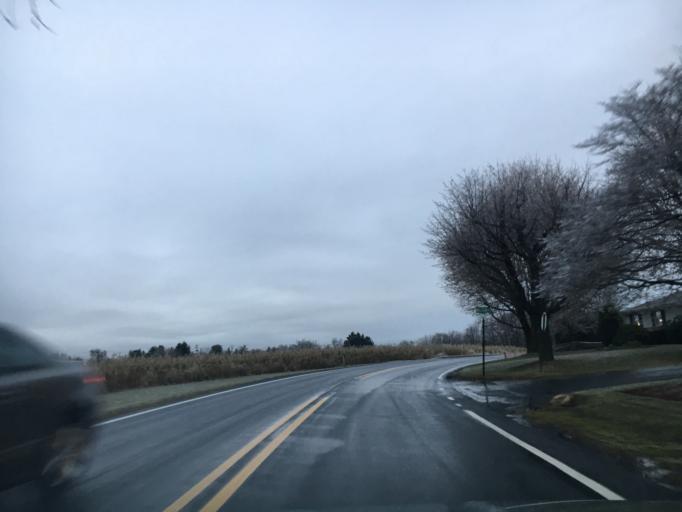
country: US
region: Pennsylvania
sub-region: Lehigh County
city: Schnecksville
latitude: 40.6449
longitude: -75.5963
